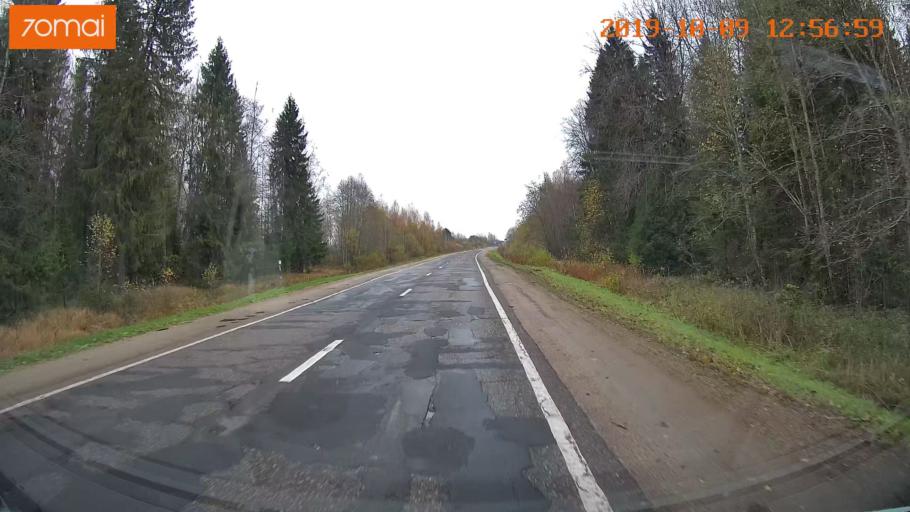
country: RU
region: Jaroslavl
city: Prechistoye
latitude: 58.3937
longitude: 40.4258
